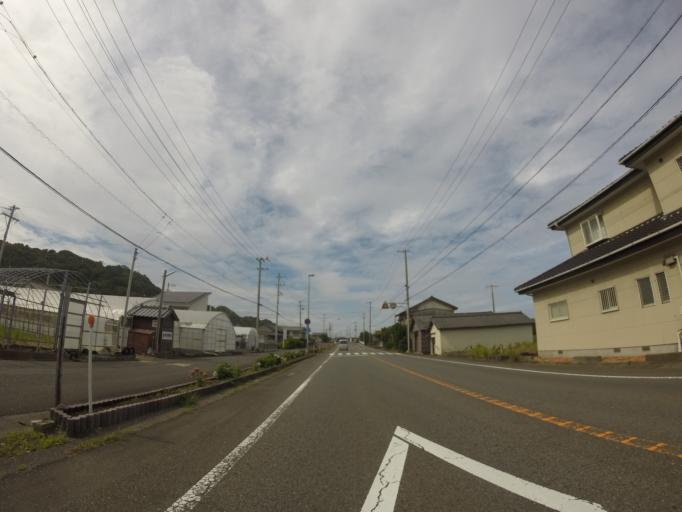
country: JP
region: Shizuoka
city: Sagara
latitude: 34.7057
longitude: 138.2130
